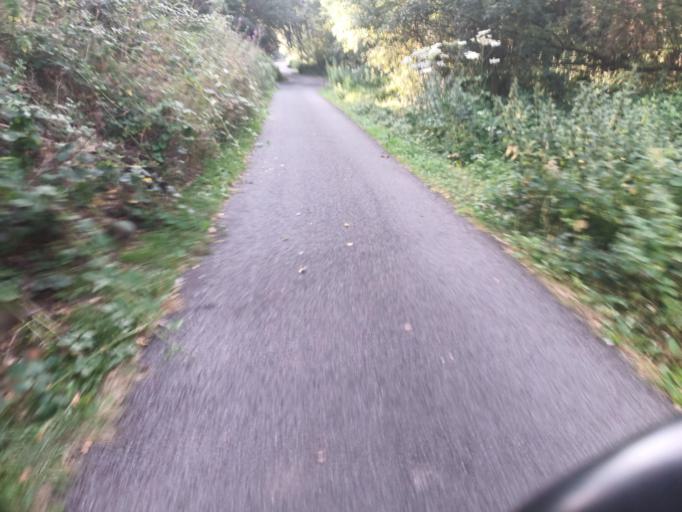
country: GB
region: Northern Ireland
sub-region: Castlereagh District
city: Dundonald
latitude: 54.5881
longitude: -5.8055
